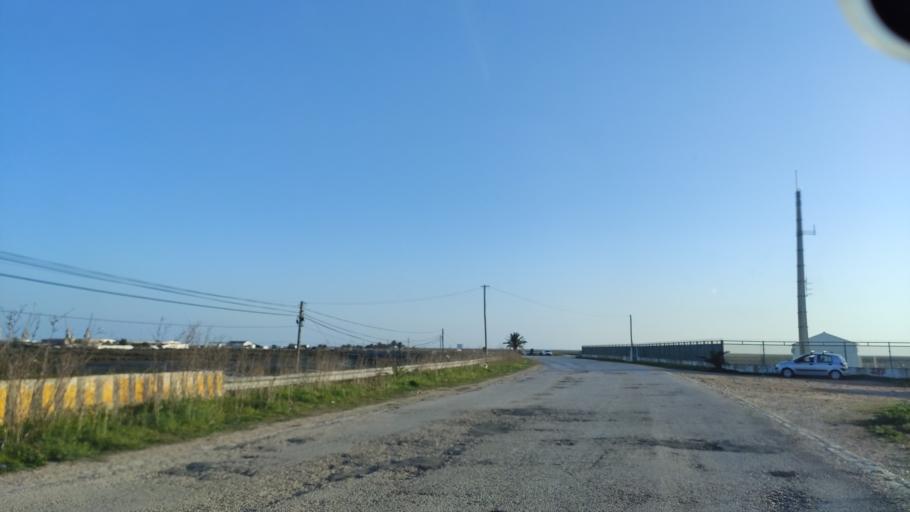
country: PT
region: Faro
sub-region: Faro
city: Faro
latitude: 37.0095
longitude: -7.9256
